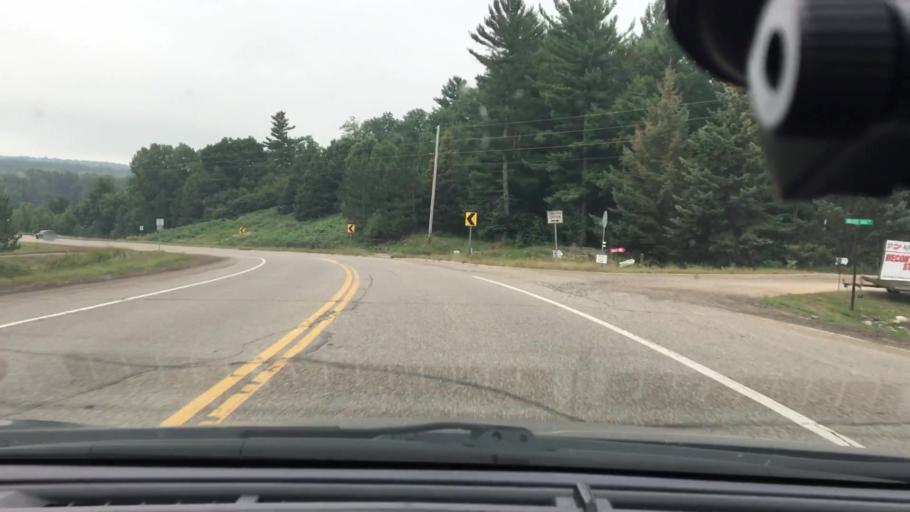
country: US
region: Minnesota
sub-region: Crow Wing County
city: Cross Lake
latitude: 46.8207
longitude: -93.9483
